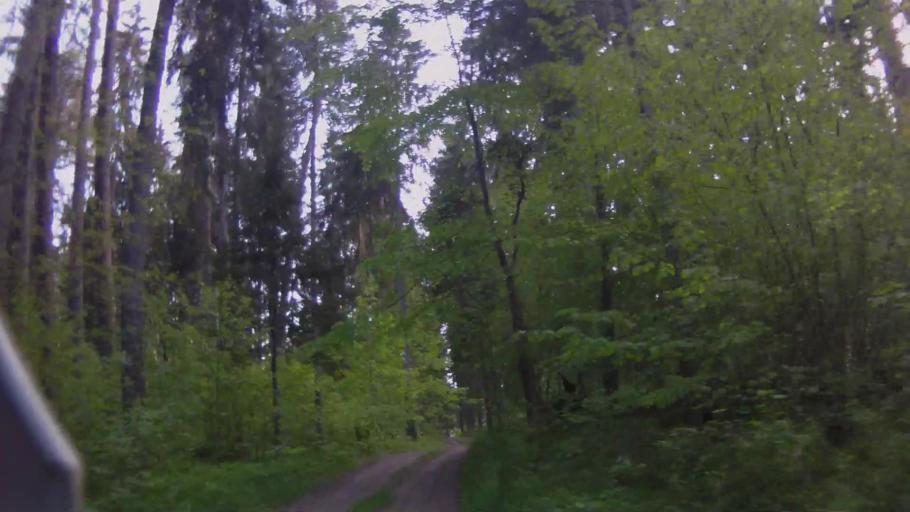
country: LV
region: Baldone
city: Baldone
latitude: 56.7436
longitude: 24.4261
